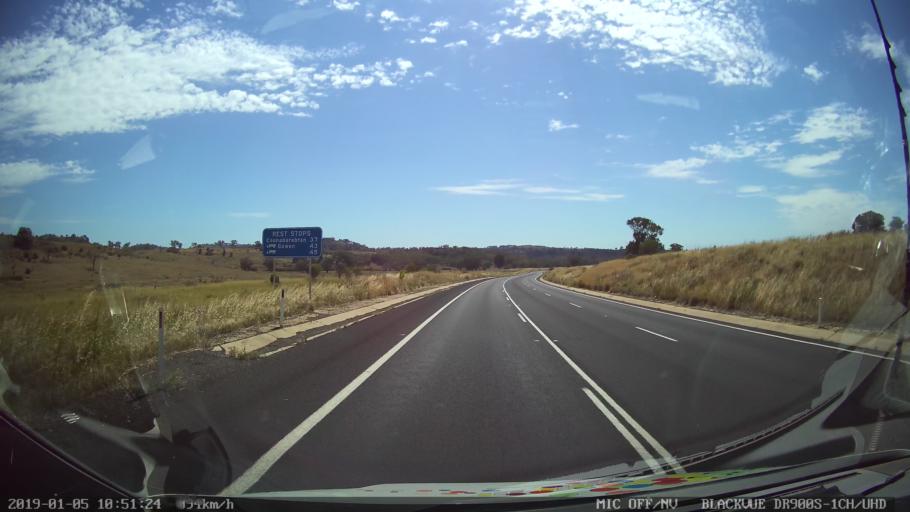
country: AU
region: New South Wales
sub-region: Warrumbungle Shire
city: Coonabarabran
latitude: -31.4253
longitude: 149.0890
